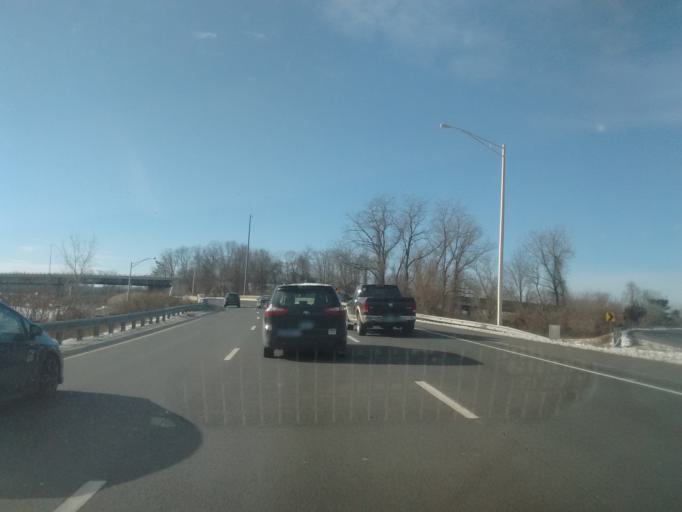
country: US
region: Connecticut
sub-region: Hartford County
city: Plainville
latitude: 41.6703
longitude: -72.8421
